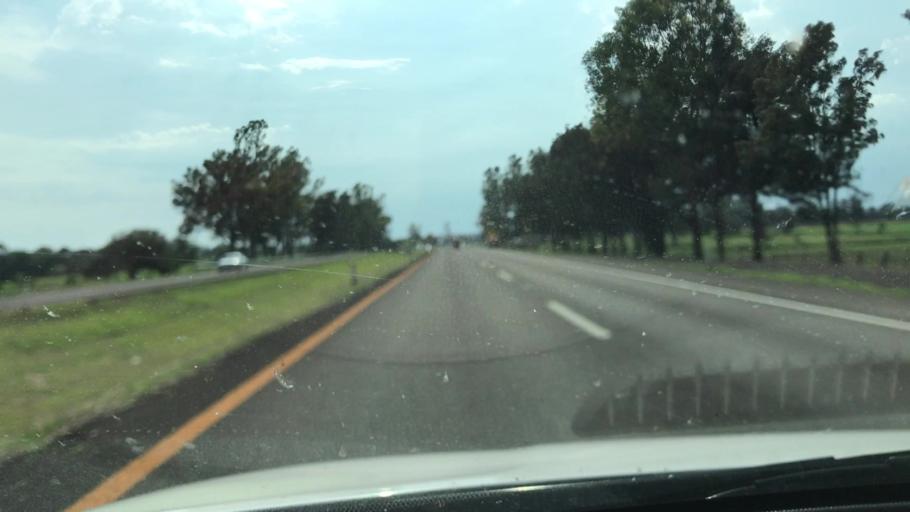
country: MX
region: Jalisco
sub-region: Ocotlan
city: Joconoxtle (La Tuna)
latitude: 20.3806
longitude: -102.6953
